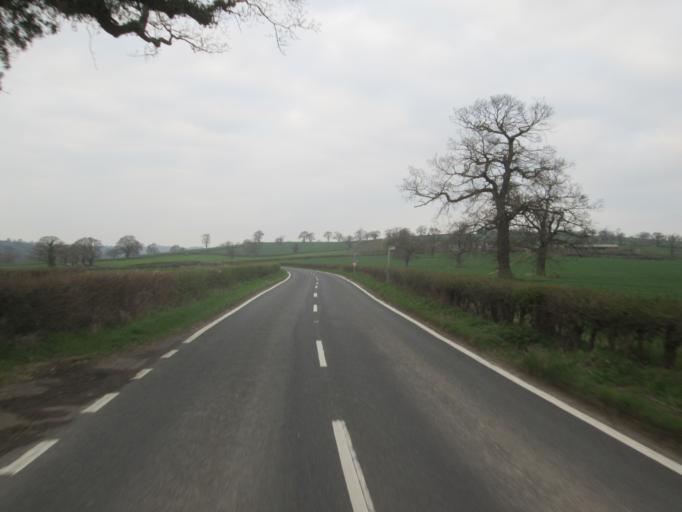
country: GB
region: England
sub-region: Derbyshire
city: Wirksworth
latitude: 53.0219
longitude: -1.5476
